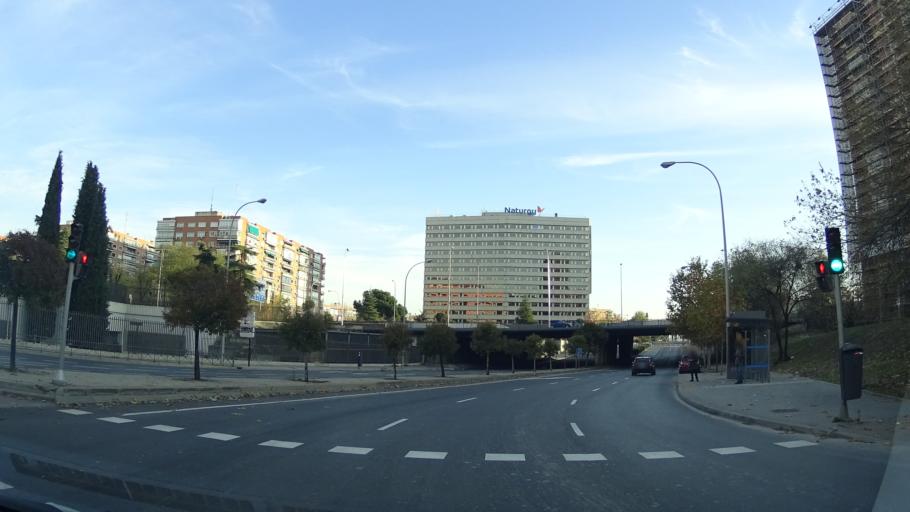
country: ES
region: Madrid
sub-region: Provincia de Madrid
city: Salamanca
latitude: 40.4429
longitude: -3.6673
